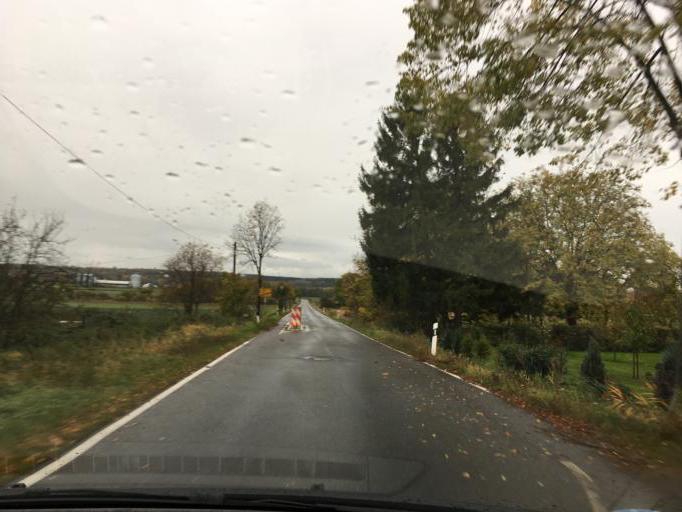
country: DE
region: North Rhine-Westphalia
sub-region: Regierungsbezirk Koln
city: Vettweiss
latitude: 50.6978
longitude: 6.5688
